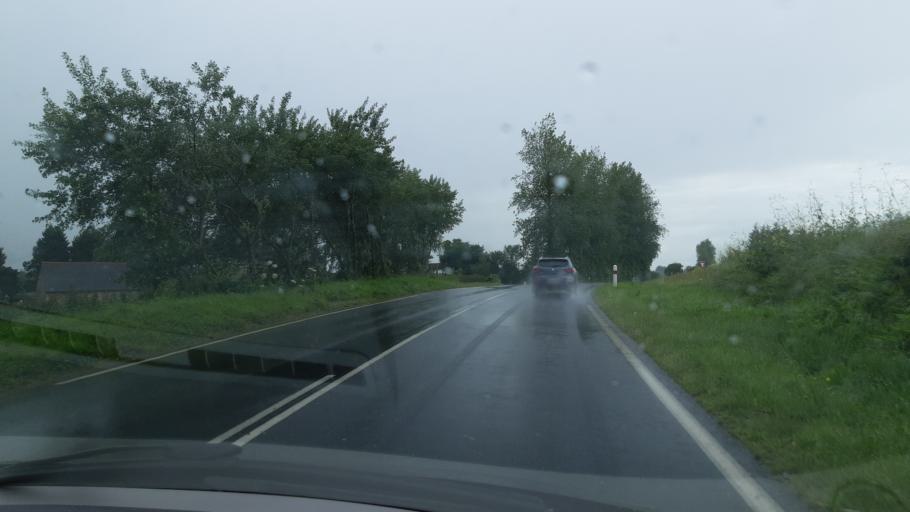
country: FR
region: Brittany
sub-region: Departement du Finistere
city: Plougoulm
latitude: 48.6522
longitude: -4.0372
